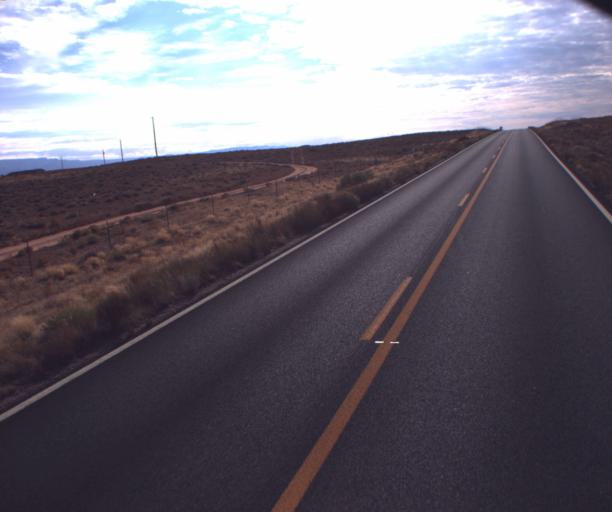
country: US
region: Arizona
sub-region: Apache County
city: Many Farms
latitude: 36.5858
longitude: -109.5586
